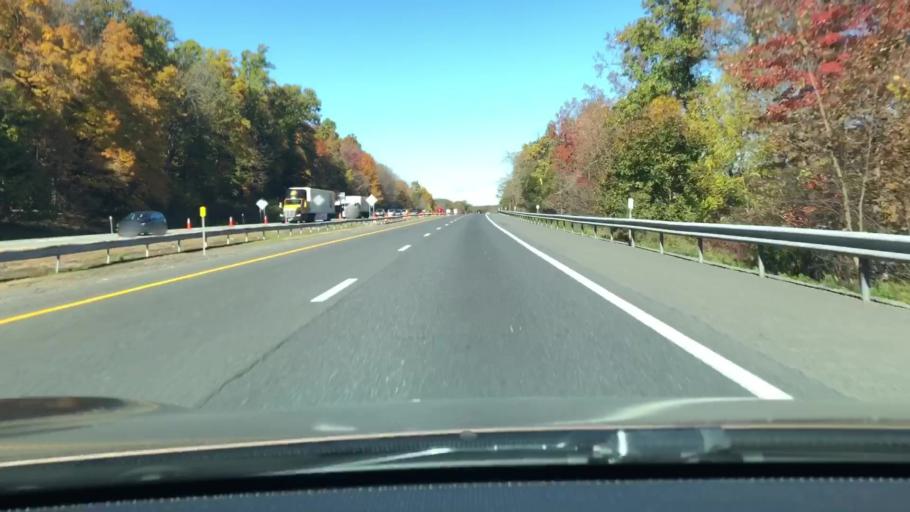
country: US
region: New York
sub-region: Orange County
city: Gardnertown
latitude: 41.5268
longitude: -74.0751
